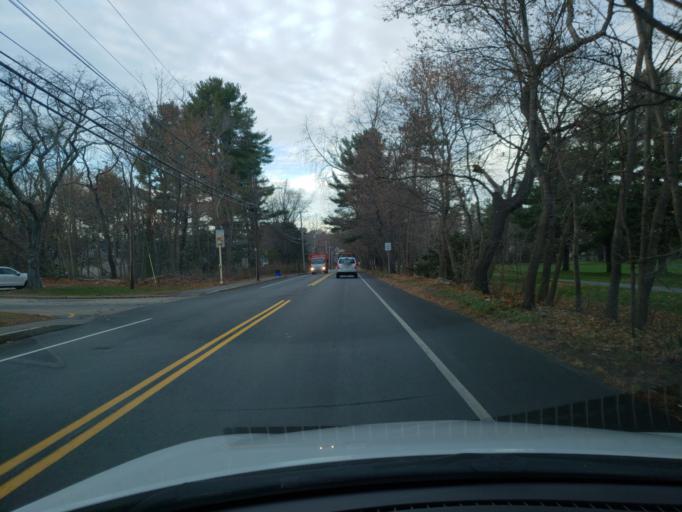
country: US
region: Massachusetts
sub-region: Essex County
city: Andover
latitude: 42.6651
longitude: -71.1707
